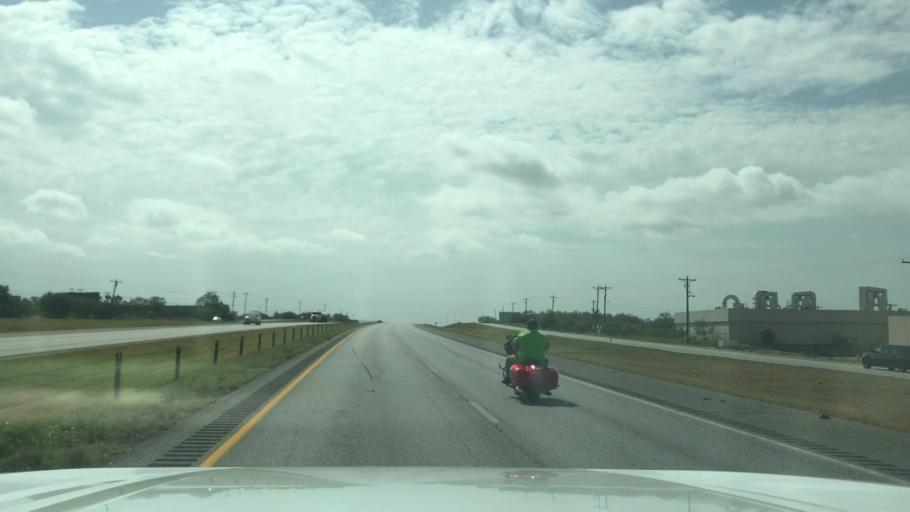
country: US
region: Texas
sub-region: Taylor County
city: Abilene
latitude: 32.4700
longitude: -99.6887
